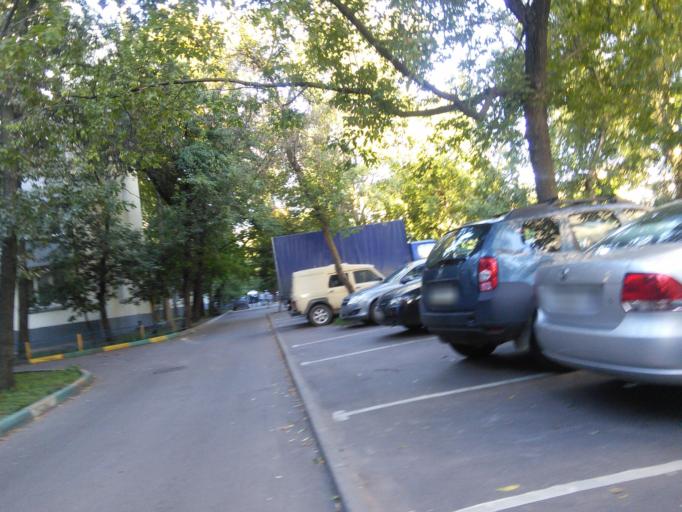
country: RU
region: Moskovskaya
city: Levoberezhnyy
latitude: 55.8460
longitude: 37.4471
